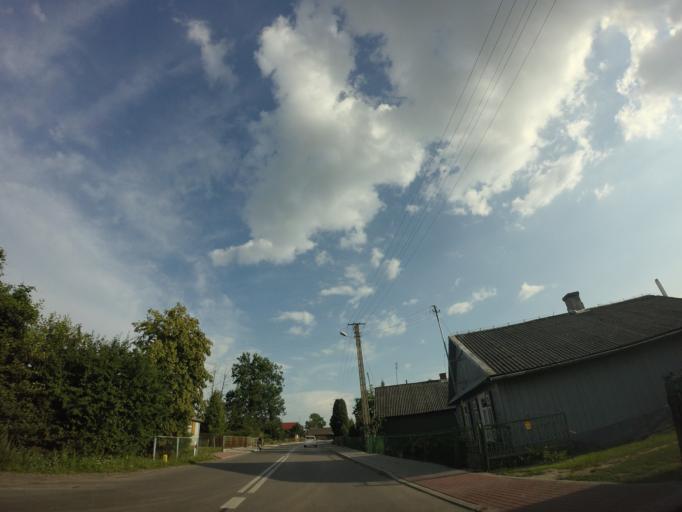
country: PL
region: Lublin Voivodeship
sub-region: Powiat lubartowski
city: Jeziorzany
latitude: 51.6070
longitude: 22.2787
